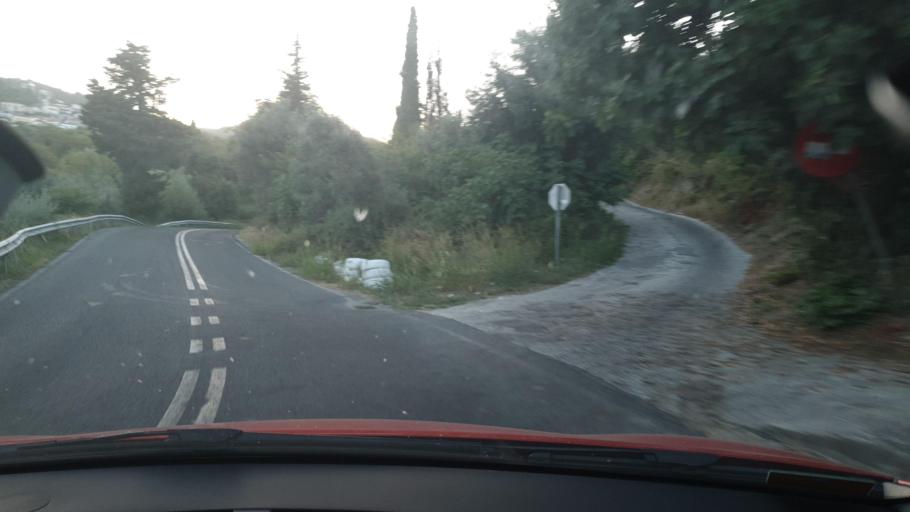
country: GR
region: Central Greece
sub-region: Nomos Evvoias
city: Kymi
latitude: 38.6310
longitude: 24.1129
